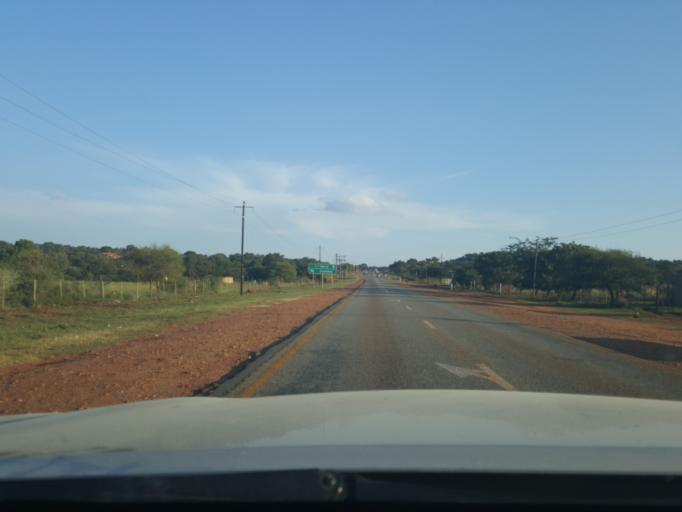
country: ZA
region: North-West
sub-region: Ngaka Modiri Molema District Municipality
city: Zeerust
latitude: -25.3123
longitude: 26.1231
